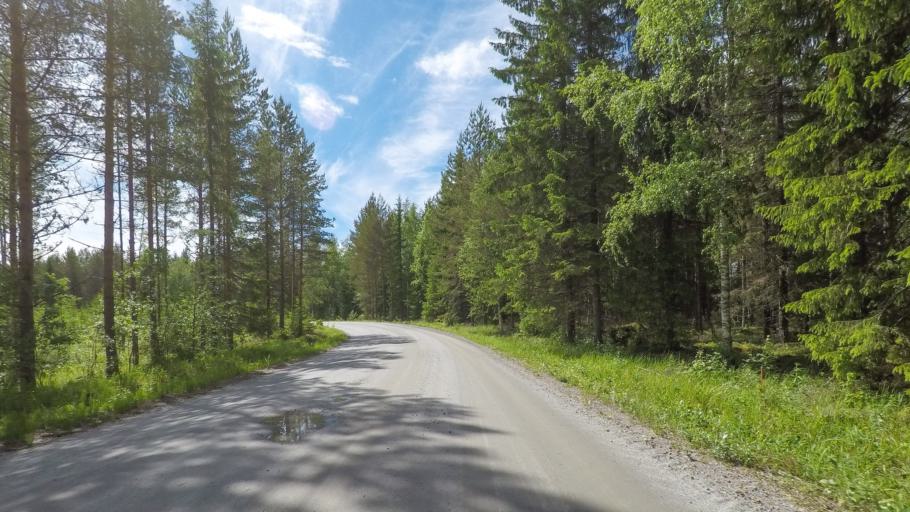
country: FI
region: Central Finland
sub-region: Jyvaeskylae
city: Hankasalmi
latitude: 62.3972
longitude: 26.5962
